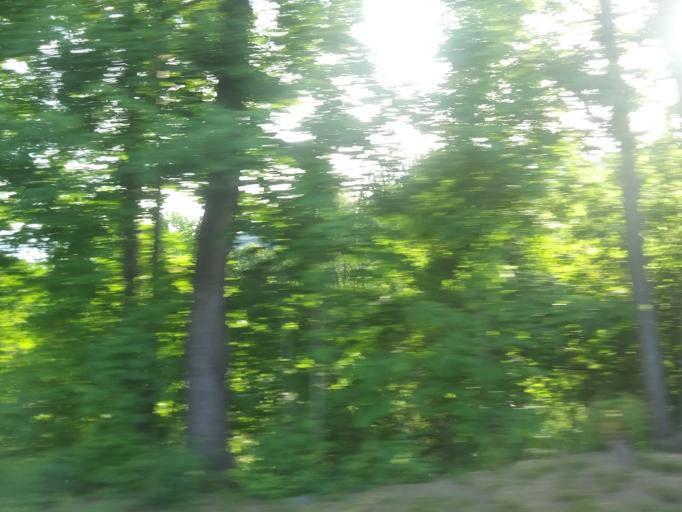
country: US
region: Massachusetts
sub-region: Franklin County
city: Shelburne Falls
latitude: 42.6007
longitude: -72.7408
